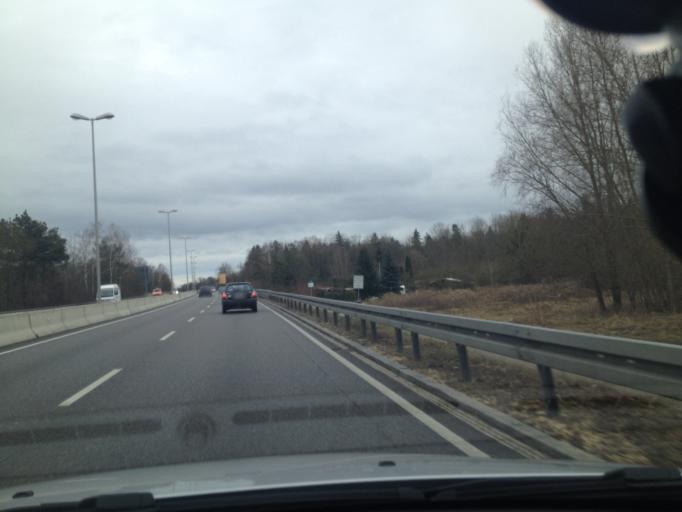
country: DE
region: Bavaria
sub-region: Swabia
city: Stadtbergen
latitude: 48.3505
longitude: 10.8618
